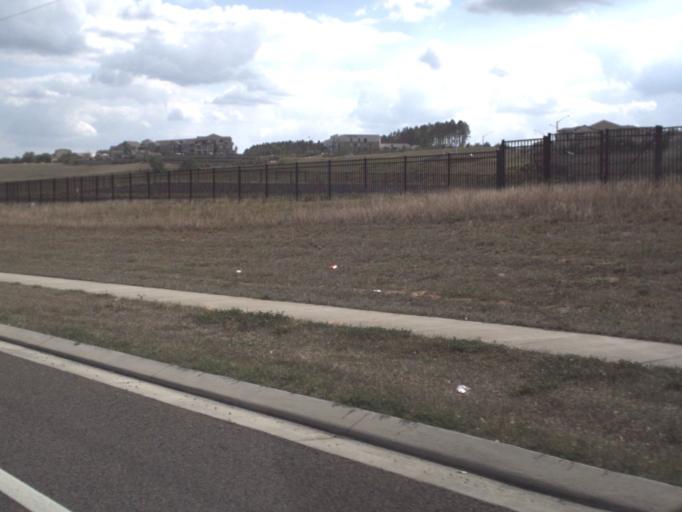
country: US
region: Florida
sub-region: Lake County
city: Clermont
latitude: 28.5190
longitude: -81.7281
